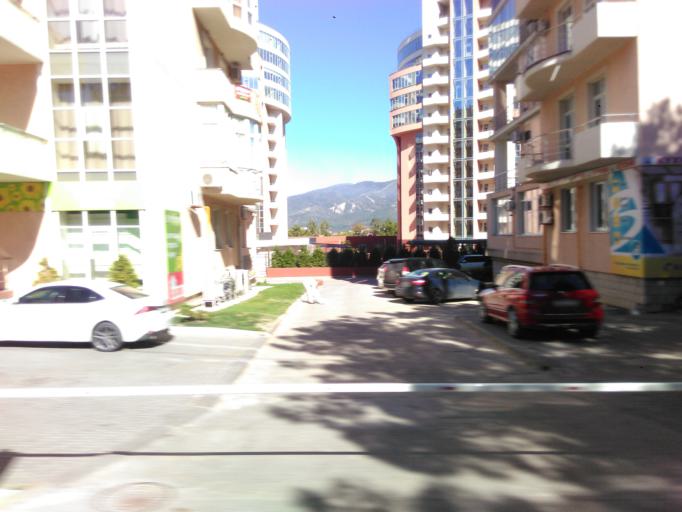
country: RU
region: Krasnodarskiy
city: Gelendzhik
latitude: 44.5529
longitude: 38.0672
